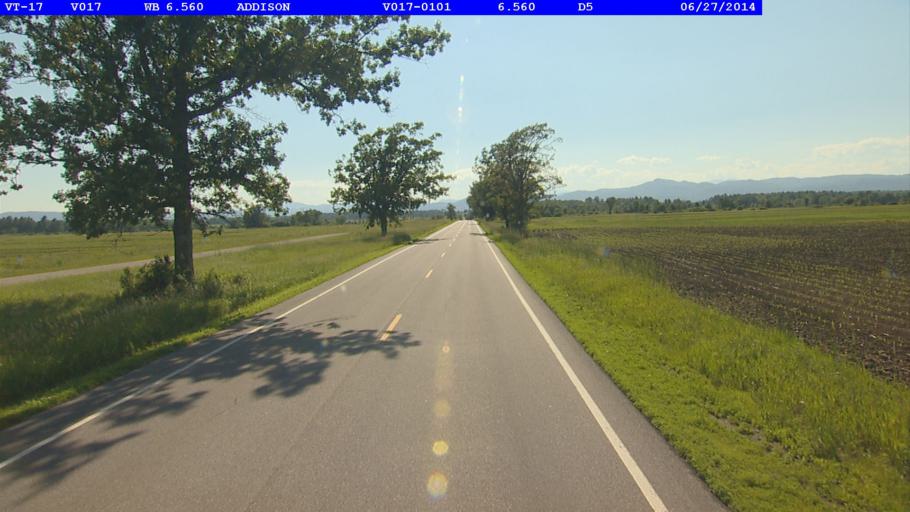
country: US
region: Vermont
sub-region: Addison County
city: Vergennes
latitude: 44.0854
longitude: -73.3386
